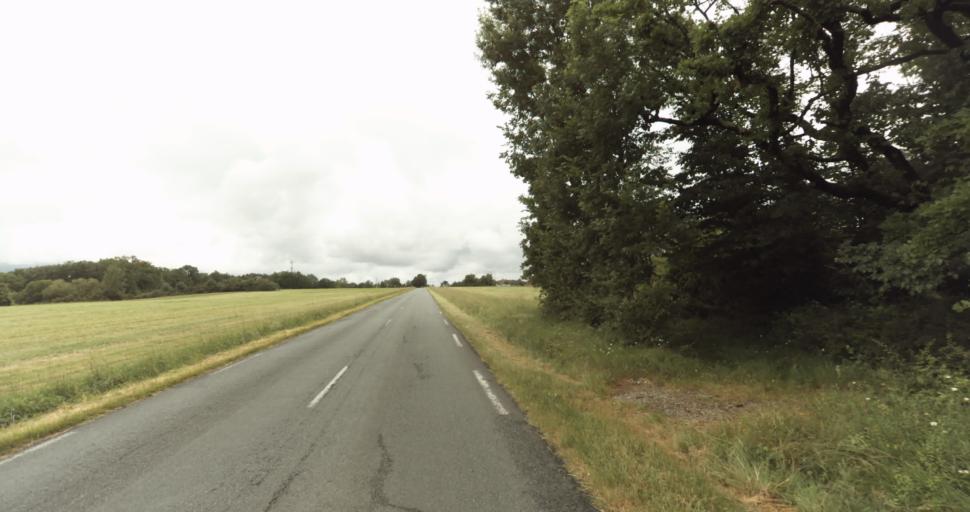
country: FR
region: Aquitaine
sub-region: Departement de la Dordogne
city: Beaumont-du-Perigord
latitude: 44.7445
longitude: 0.7805
